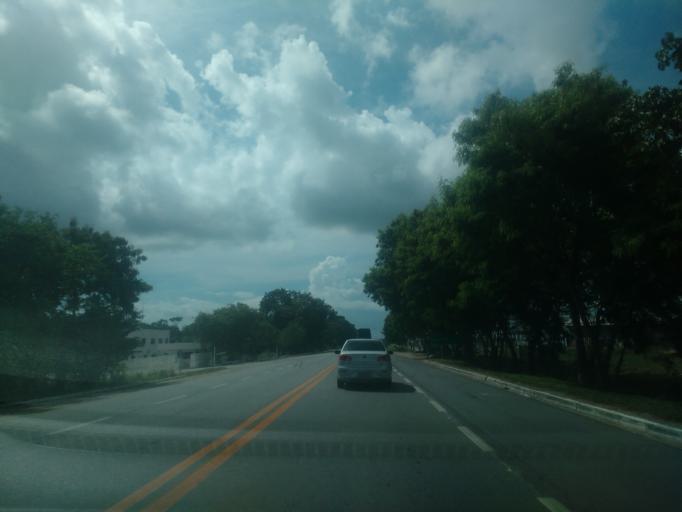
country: BR
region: Alagoas
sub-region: Marechal Deodoro
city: Marechal Deodoro
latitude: -9.6810
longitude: -35.8306
